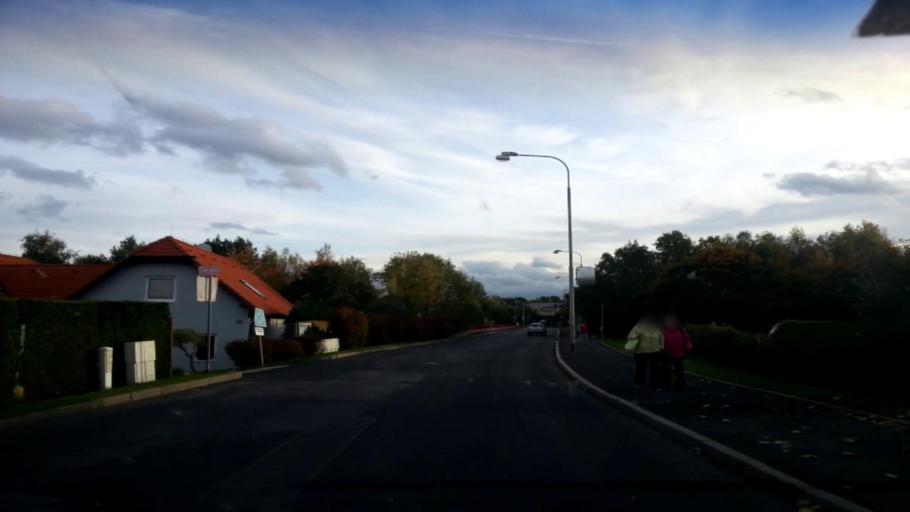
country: CZ
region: Karlovarsky
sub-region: Okres Cheb
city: Cheb
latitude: 50.0640
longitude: 12.3710
